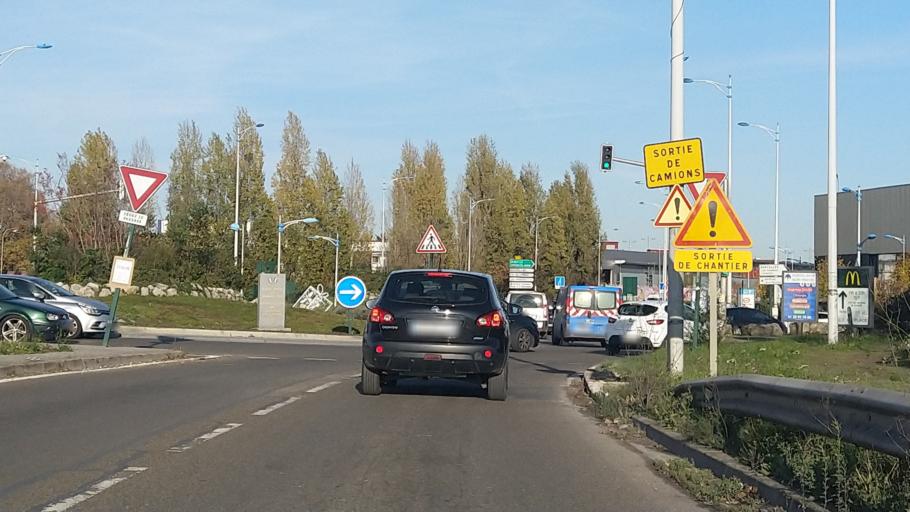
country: FR
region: Ile-de-France
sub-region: Departement de Seine-Saint-Denis
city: Pierrefitte-sur-Seine
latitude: 48.9821
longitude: 2.3704
